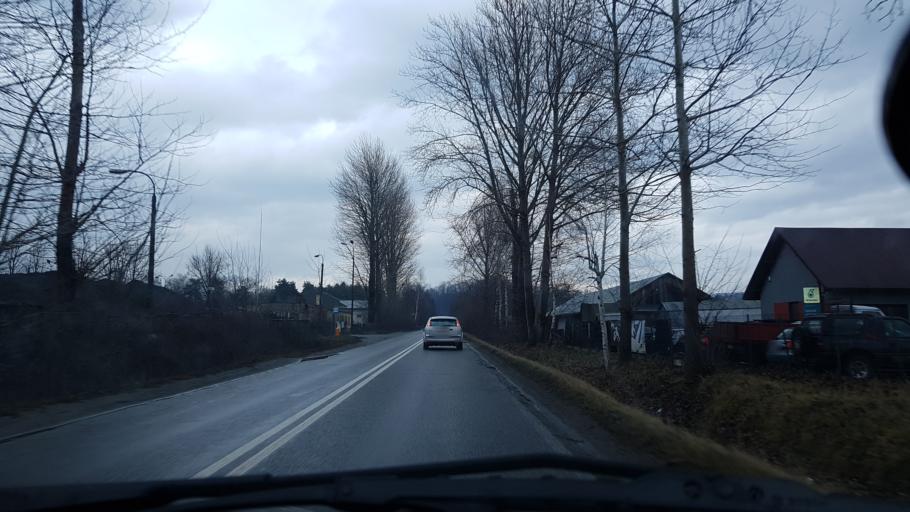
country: PL
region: Silesian Voivodeship
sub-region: Powiat zywiecki
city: Lekawica
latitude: 49.7114
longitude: 19.2520
